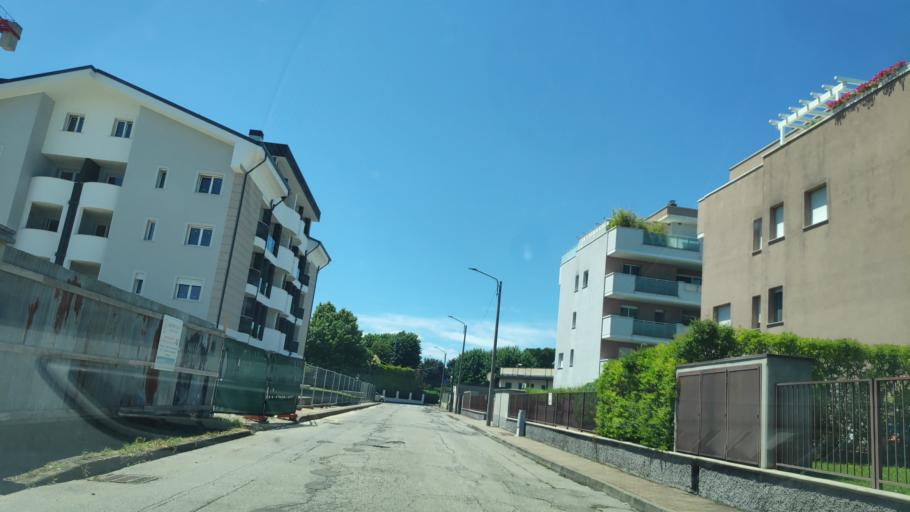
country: IT
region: Lombardy
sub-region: Citta metropolitana di Milano
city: Civesio
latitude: 45.3961
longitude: 9.2506
